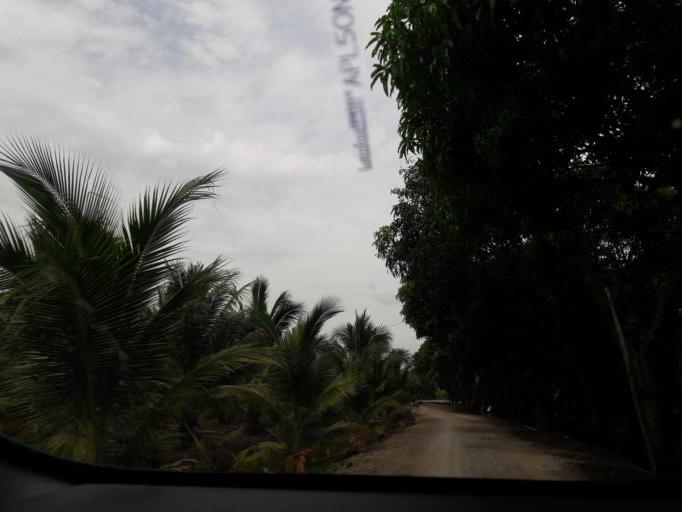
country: TH
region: Ratchaburi
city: Damnoen Saduak
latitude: 13.5606
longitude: 99.9860
